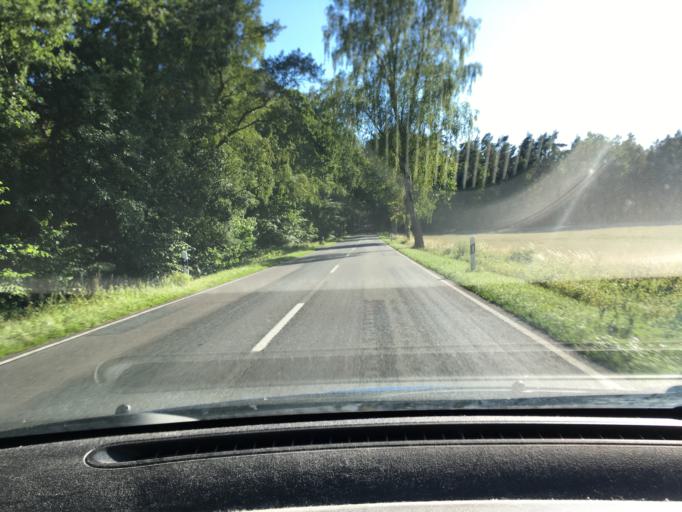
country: DE
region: Lower Saxony
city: Rullstorf
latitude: 53.2575
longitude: 10.5360
